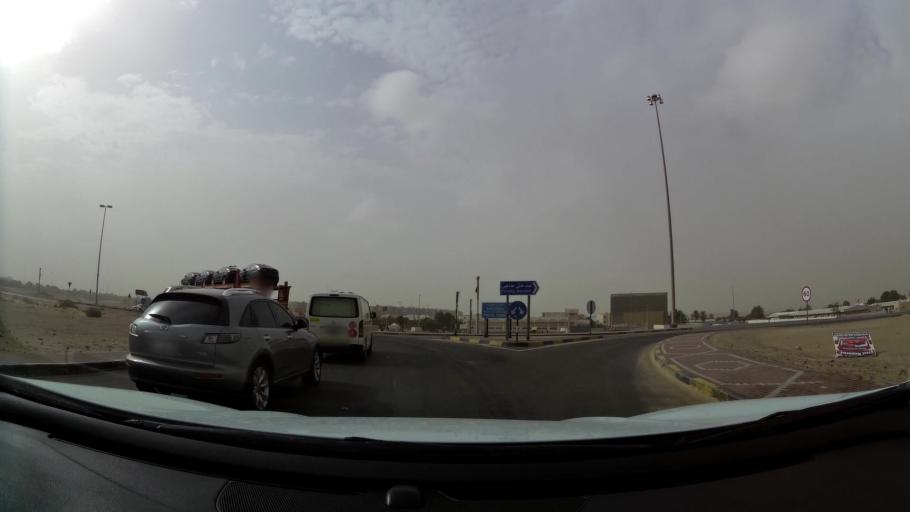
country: AE
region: Abu Dhabi
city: Abu Dhabi
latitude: 24.4642
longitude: 54.6740
